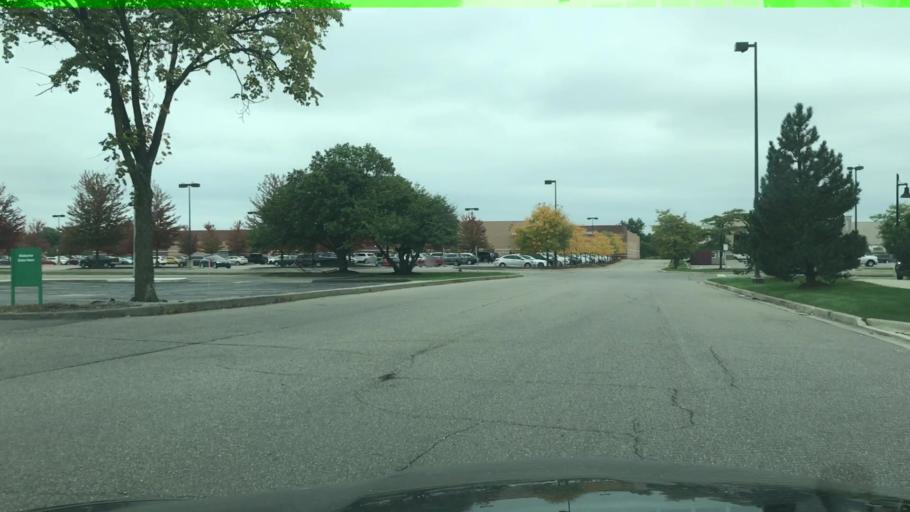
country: US
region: Michigan
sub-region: Macomb County
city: Sterling Heights
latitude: 42.5637
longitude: -83.0858
